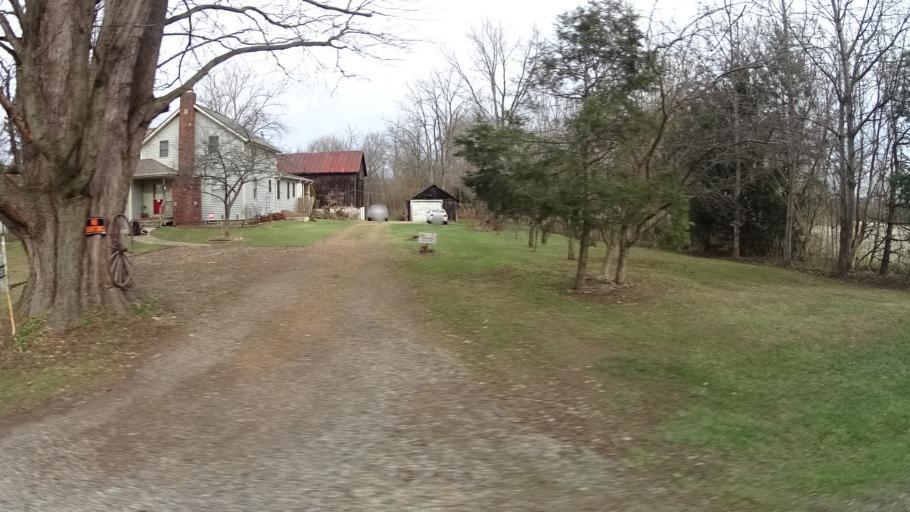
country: US
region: Ohio
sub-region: Lorain County
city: Lagrange
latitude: 41.1366
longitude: -82.1126
